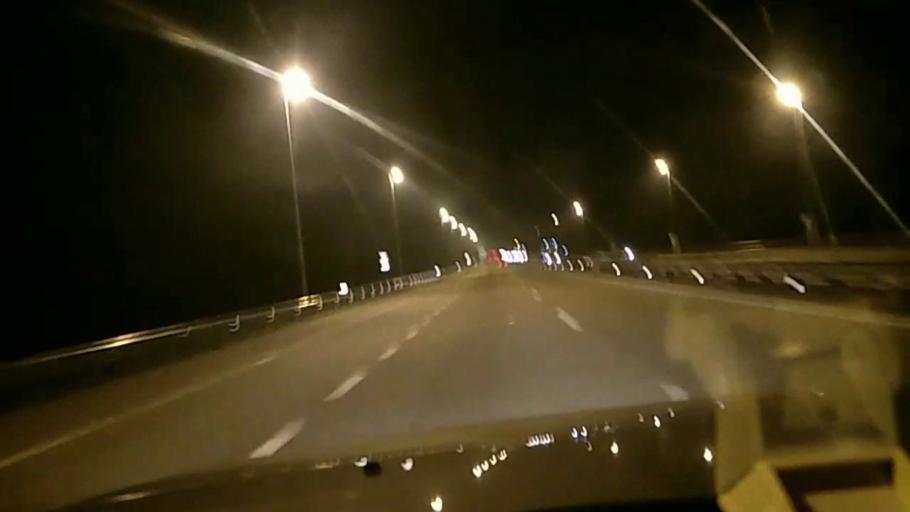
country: MY
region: Penang
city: Juru
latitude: 5.2541
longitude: 100.4677
